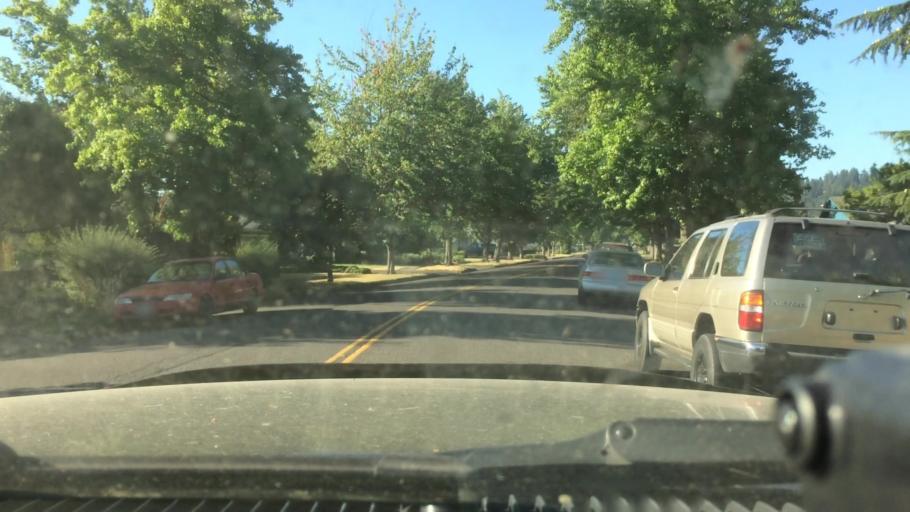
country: US
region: Oregon
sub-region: Lane County
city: Eugene
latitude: 44.0393
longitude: -123.1123
